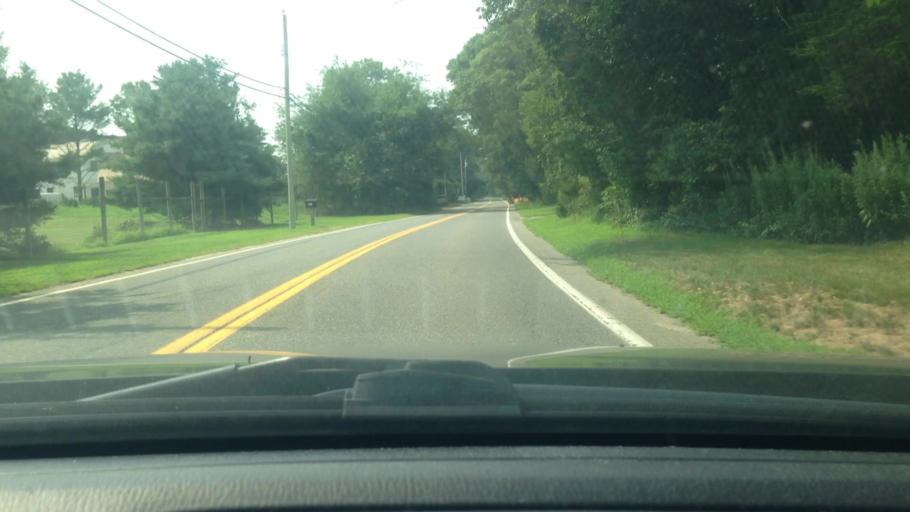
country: US
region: New York
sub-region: Suffolk County
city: Water Mill
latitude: 40.9337
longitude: -72.3409
